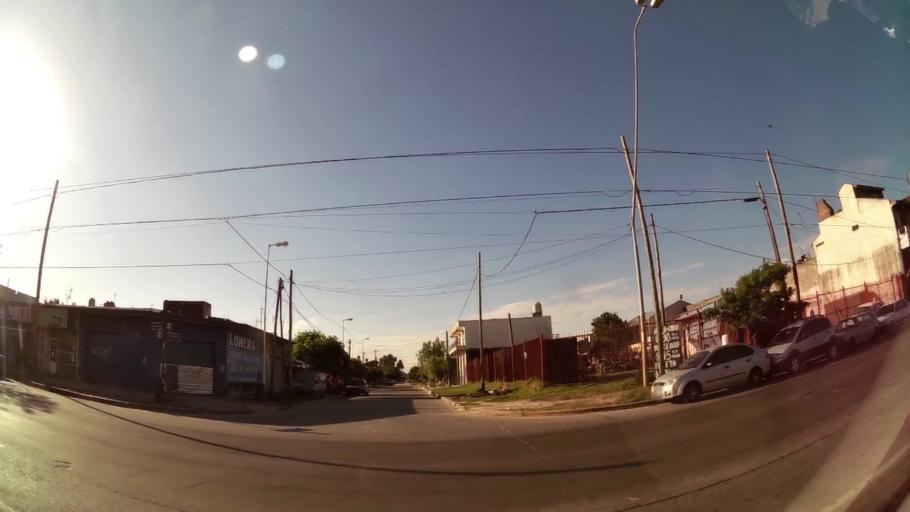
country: AR
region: Buenos Aires
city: Hurlingham
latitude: -34.5031
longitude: -58.7152
